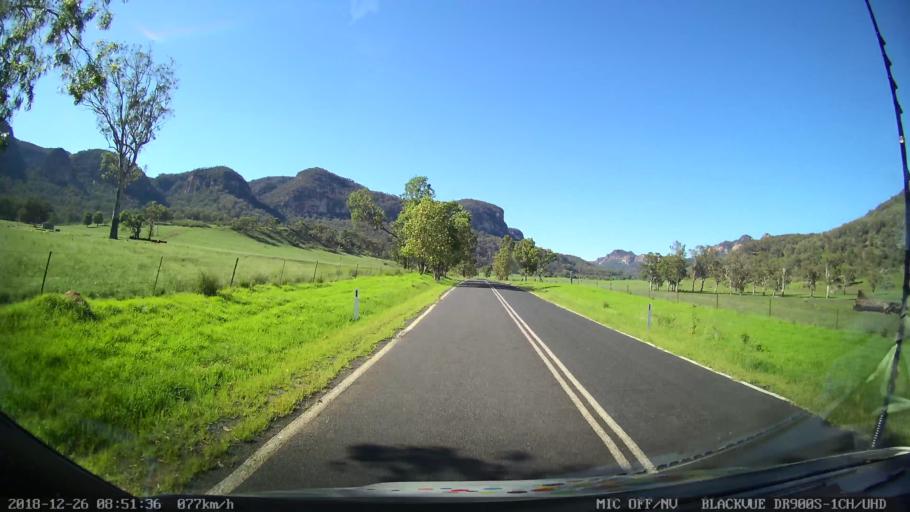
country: AU
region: New South Wales
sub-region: Mid-Western Regional
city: Kandos
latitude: -32.5872
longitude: 150.0884
